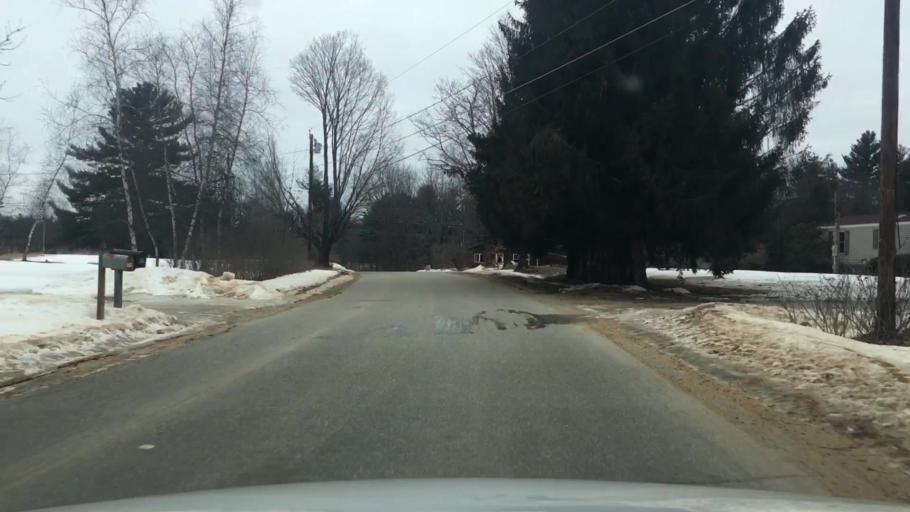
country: US
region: New Hampshire
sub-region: Strafford County
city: Rochester
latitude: 43.3610
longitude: -70.9684
